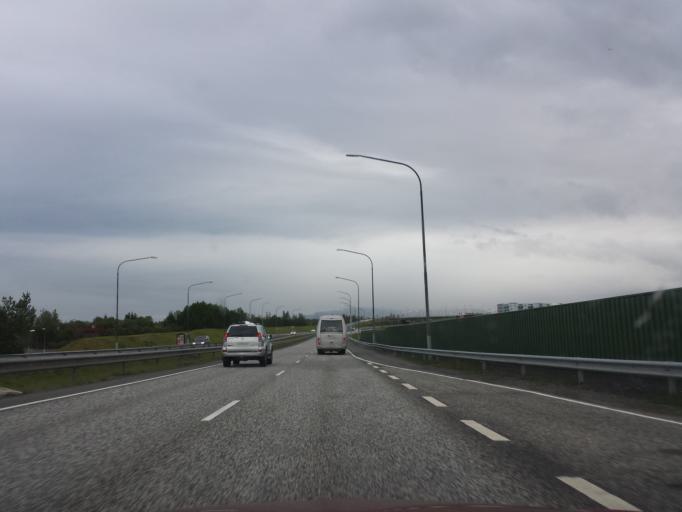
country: IS
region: Capital Region
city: Gardabaer
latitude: 64.0952
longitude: -21.9223
